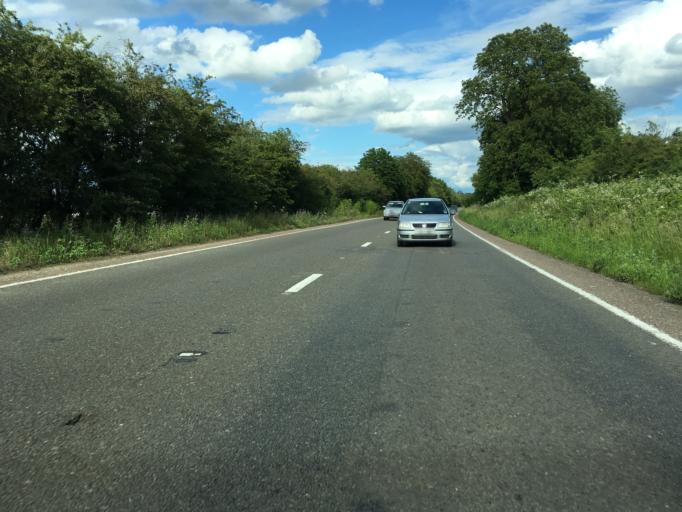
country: GB
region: England
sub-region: Oxfordshire
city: Cowley
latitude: 51.7631
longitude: -1.1791
